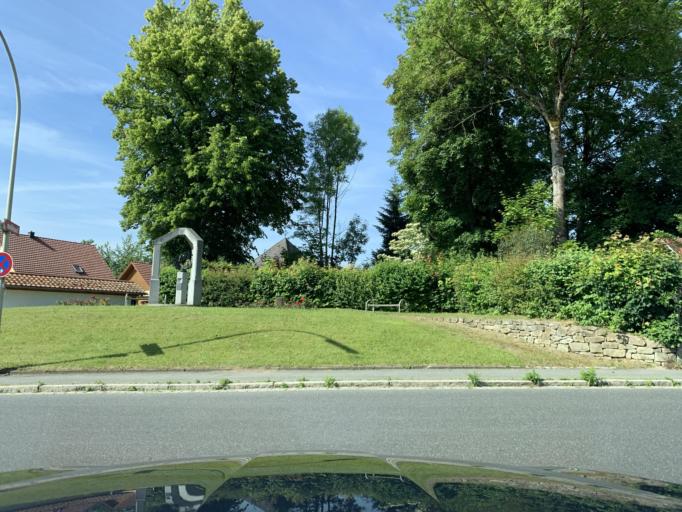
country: DE
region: Bavaria
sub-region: Upper Palatinate
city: Oberviechtach
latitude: 49.4606
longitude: 12.4157
